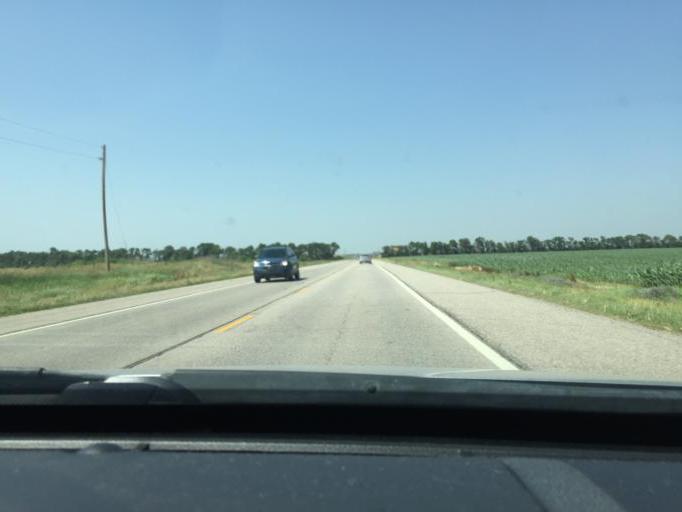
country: US
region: Kansas
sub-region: Reno County
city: South Hutchinson
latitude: 38.0169
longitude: -97.8668
